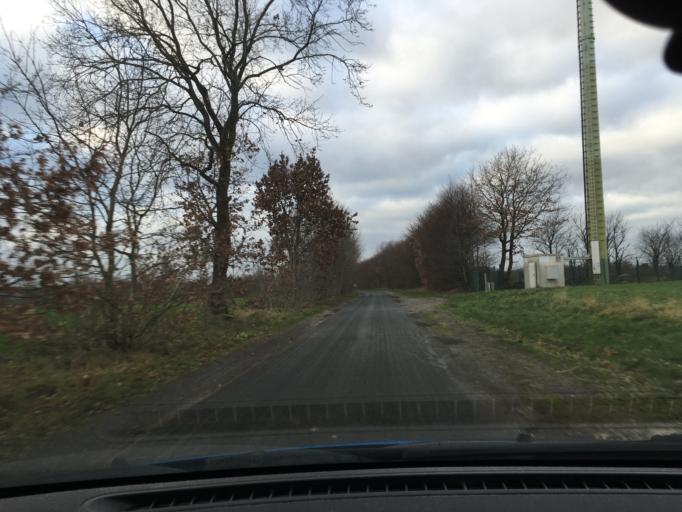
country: DE
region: Schleswig-Holstein
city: Hadenfeld
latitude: 54.0272
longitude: 9.4676
